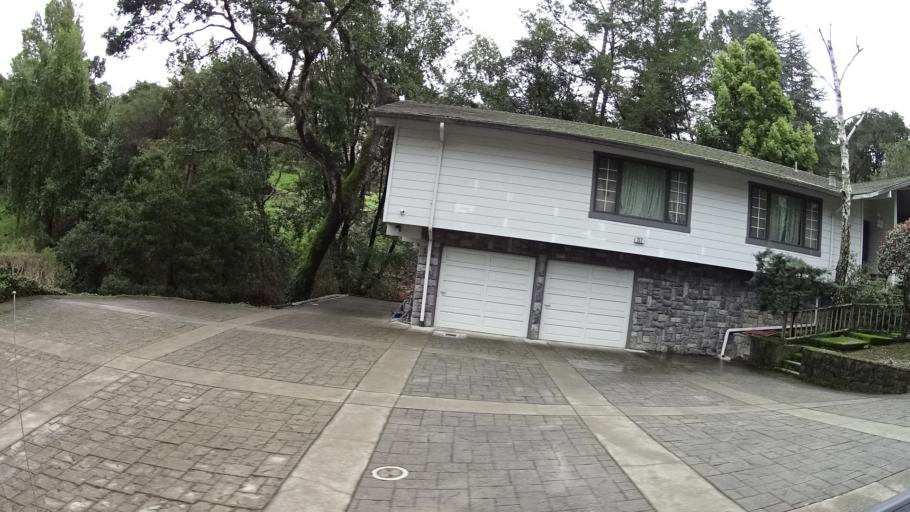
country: US
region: California
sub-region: San Mateo County
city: Hillsborough
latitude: 37.5566
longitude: -122.3750
